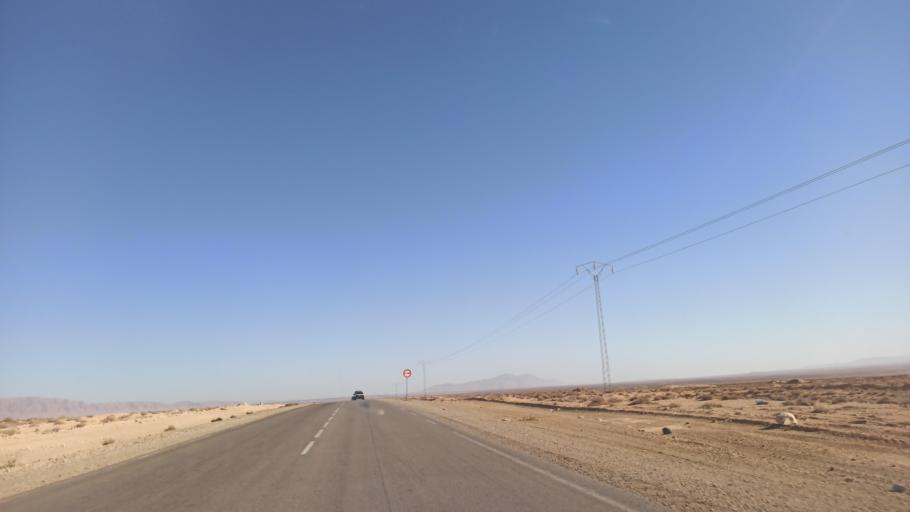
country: TN
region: Gafsa
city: Al Metlaoui
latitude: 34.3265
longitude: 8.5405
